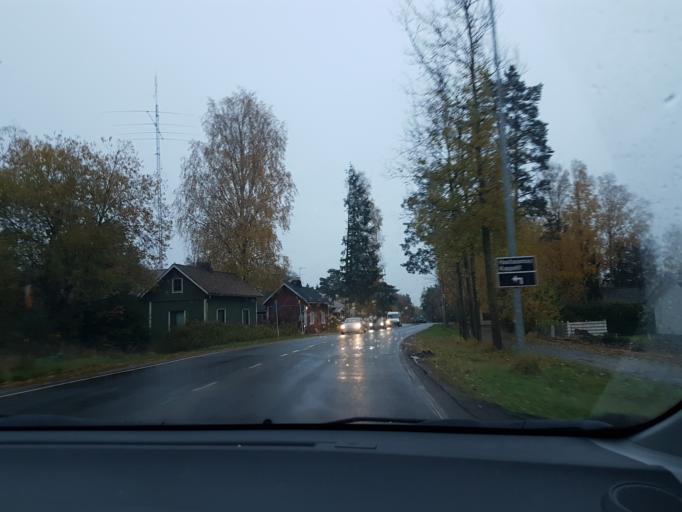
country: FI
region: Uusimaa
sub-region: Helsinki
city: Tuusula
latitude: 60.4060
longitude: 25.0099
